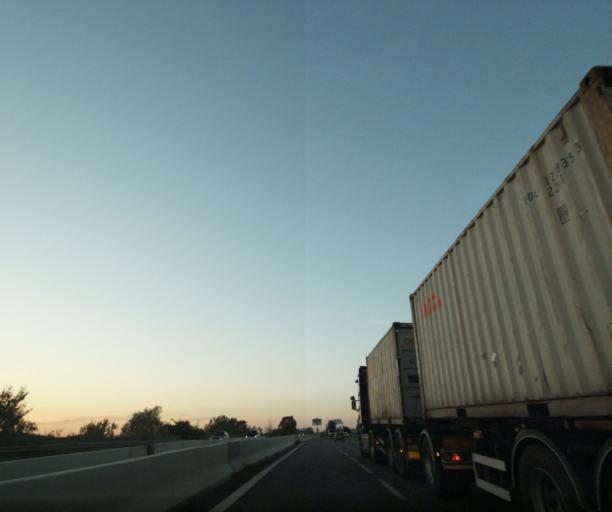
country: FR
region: Provence-Alpes-Cote d'Azur
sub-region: Departement des Bouches-du-Rhone
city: Arles
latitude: 43.6635
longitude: 4.6347
